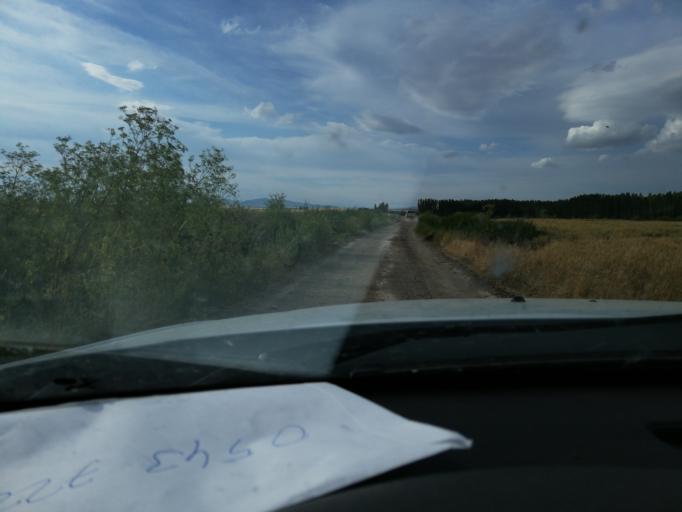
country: TR
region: Kirsehir
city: Kirsehir
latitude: 38.9982
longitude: 34.1248
